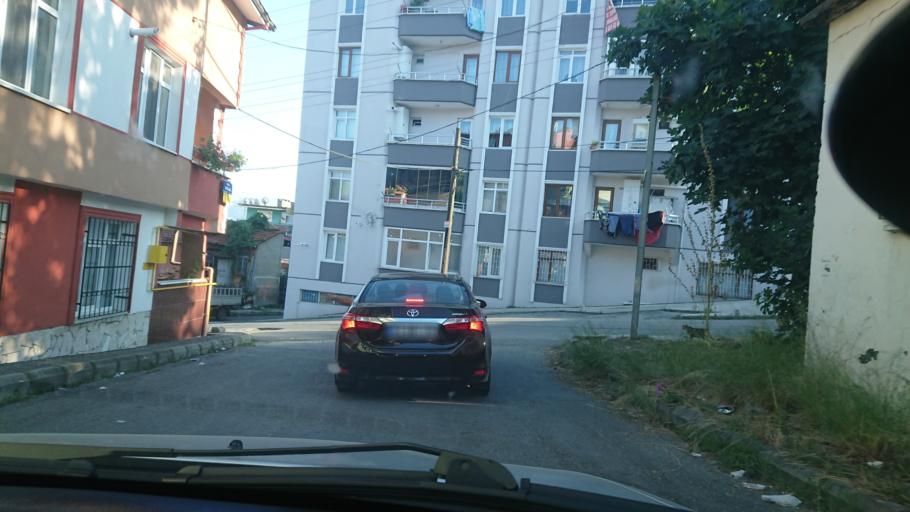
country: TR
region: Samsun
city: Samsun
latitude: 41.2974
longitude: 36.3212
